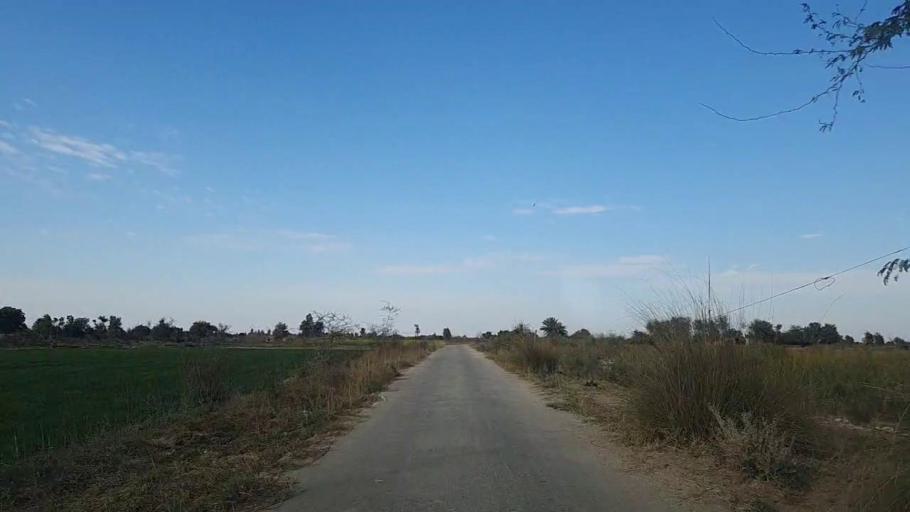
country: PK
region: Sindh
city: Khadro
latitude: 26.2848
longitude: 68.8199
